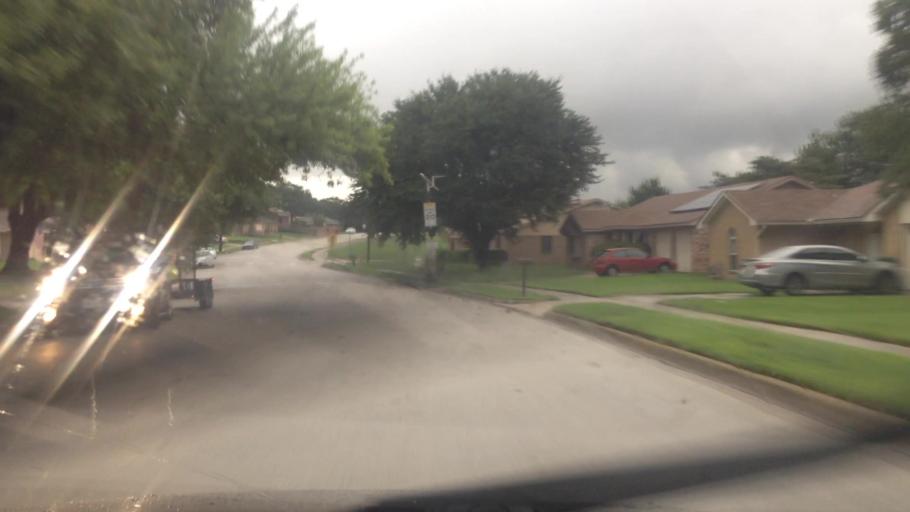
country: US
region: Texas
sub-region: Tarrant County
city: Colleyville
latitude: 32.8675
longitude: -97.1850
